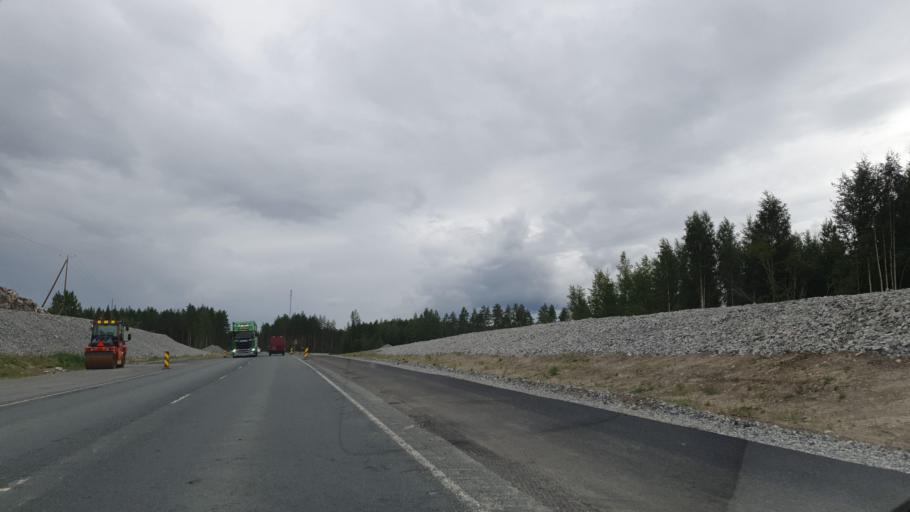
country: FI
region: Northern Savo
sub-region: Ylae-Savo
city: Lapinlahti
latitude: 63.2821
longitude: 27.4556
